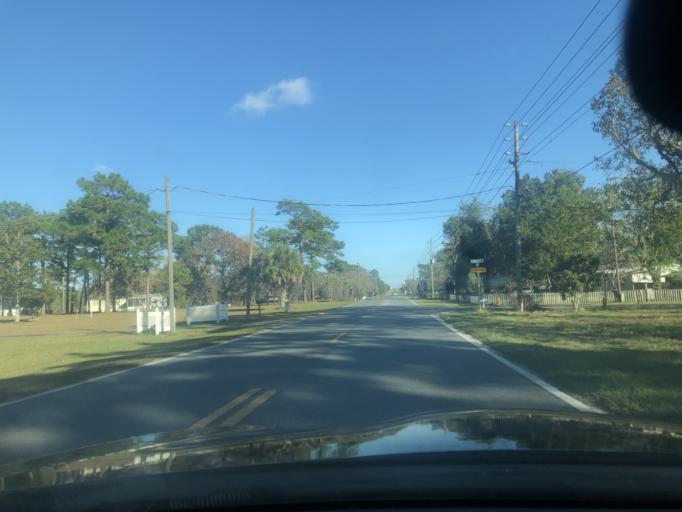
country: US
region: Florida
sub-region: Citrus County
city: Sugarmill Woods
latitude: 28.7640
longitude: -82.5340
